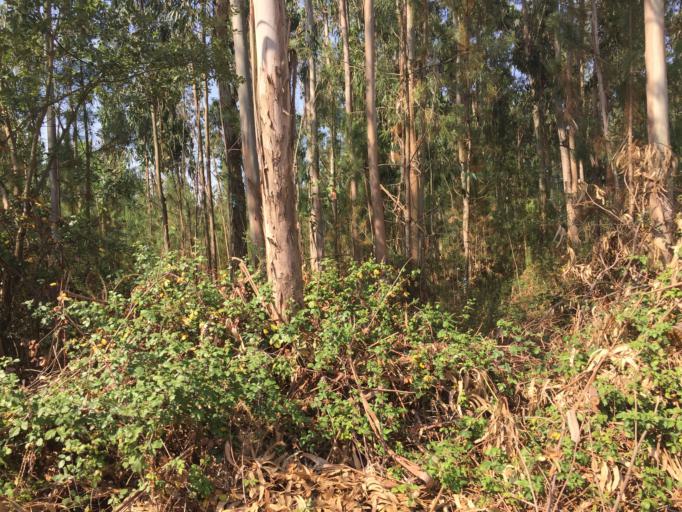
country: PT
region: Coimbra
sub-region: Cantanhede
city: Cantanhede
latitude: 40.4277
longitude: -8.5464
